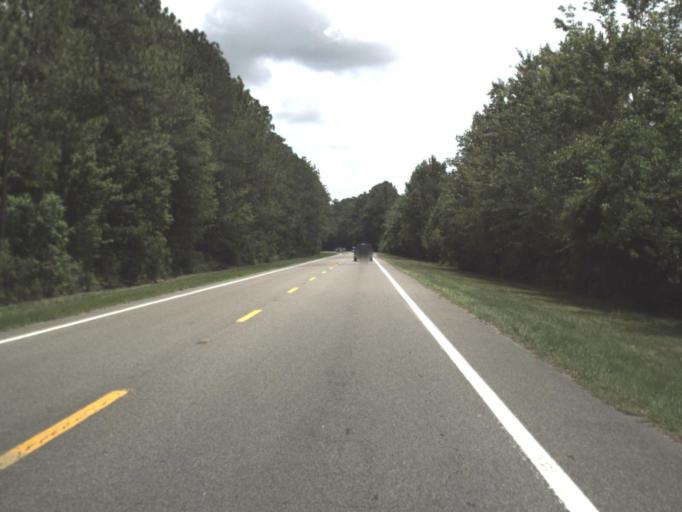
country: US
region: Florida
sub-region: Nassau County
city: Yulee
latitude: 30.6541
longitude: -81.6270
